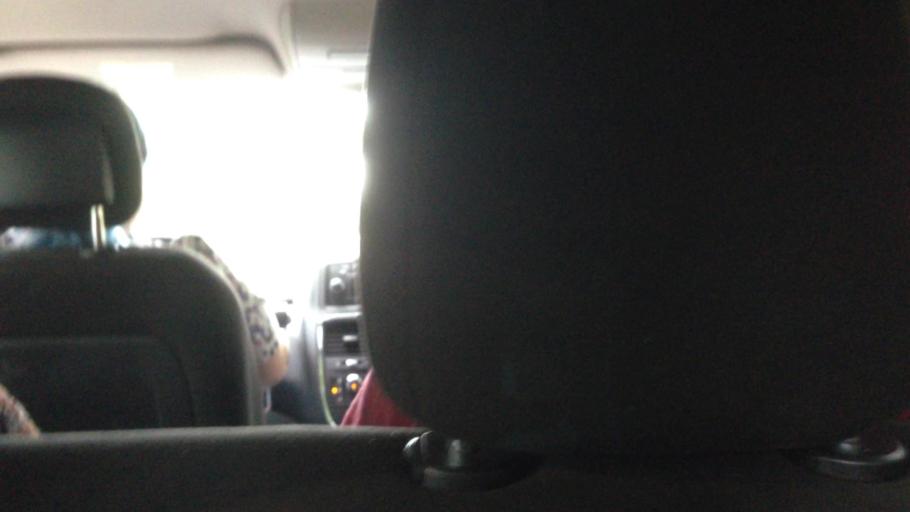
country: US
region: New York
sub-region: Dutchess County
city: Red Hook
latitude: 41.9965
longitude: -73.9105
